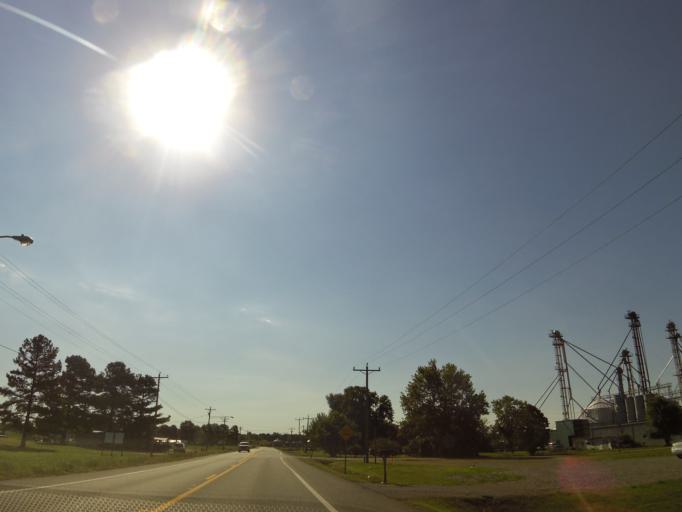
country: US
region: Arkansas
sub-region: Clay County
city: Corning
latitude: 36.4043
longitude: -90.5621
